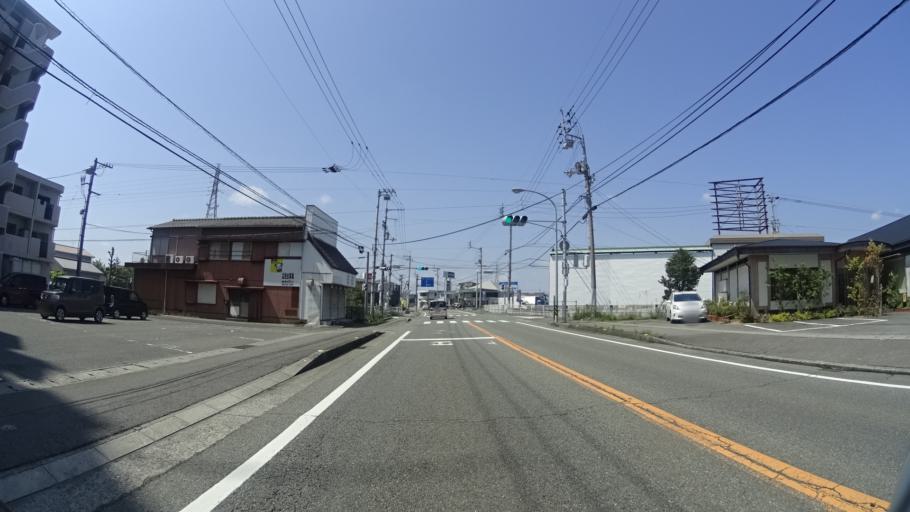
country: JP
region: Tokushima
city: Narutocho-mitsuishi
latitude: 34.1622
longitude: 134.5941
